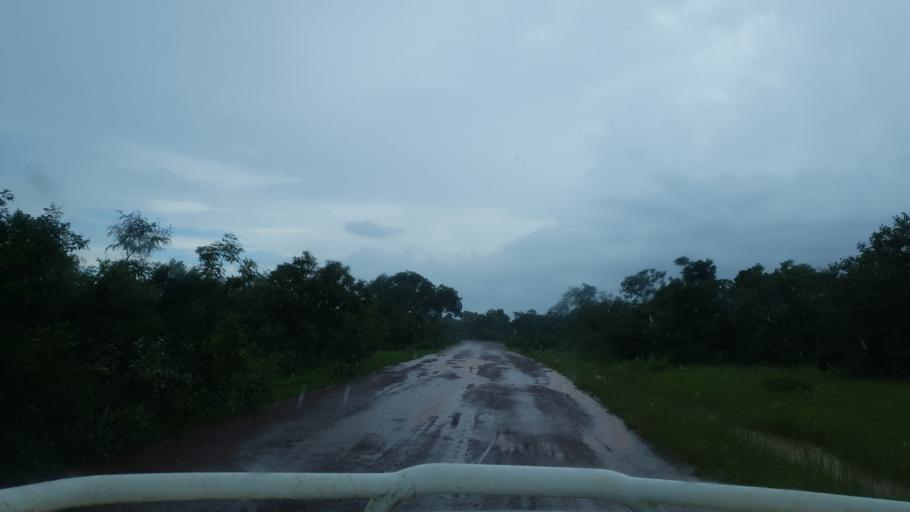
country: ML
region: Sikasso
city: Kolondieba
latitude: 11.6008
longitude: -6.6702
